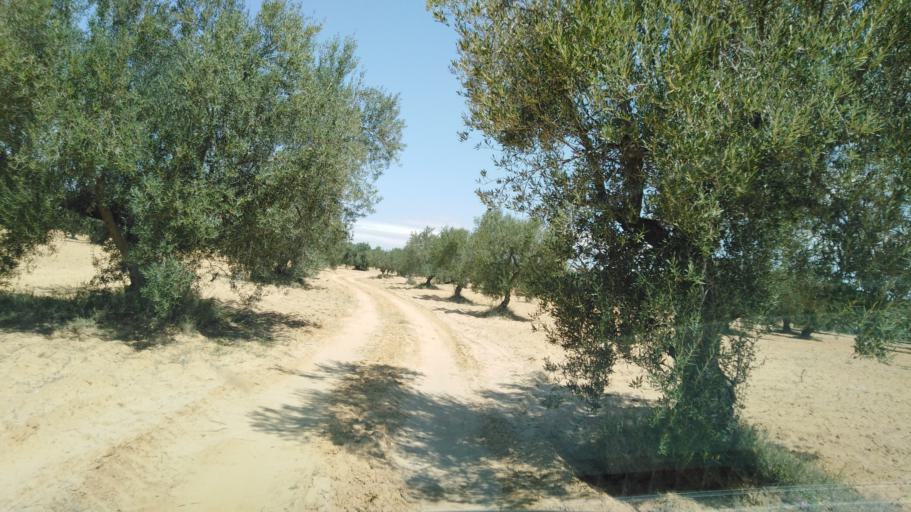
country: TN
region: Safaqis
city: Sfax
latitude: 34.7834
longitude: 10.5276
